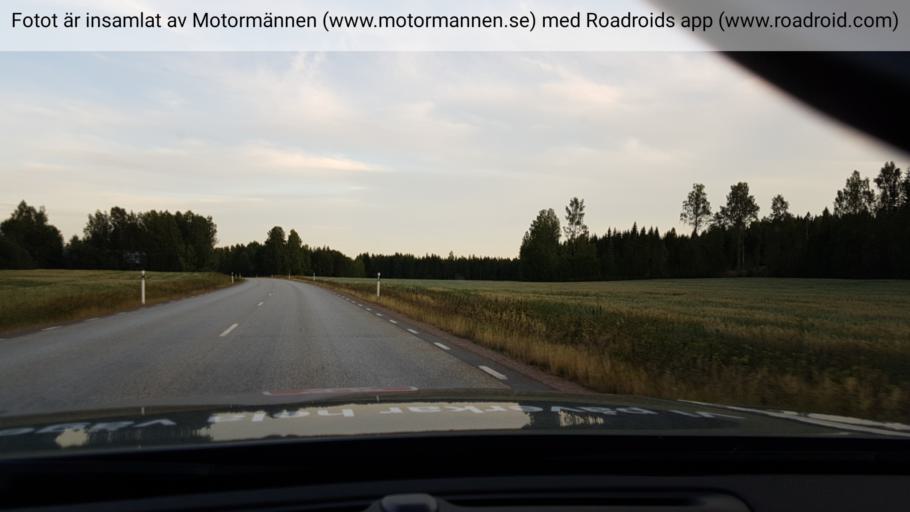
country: SE
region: Vaermland
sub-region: Storfors Kommun
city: Storfors
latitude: 59.5156
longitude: 14.3029
